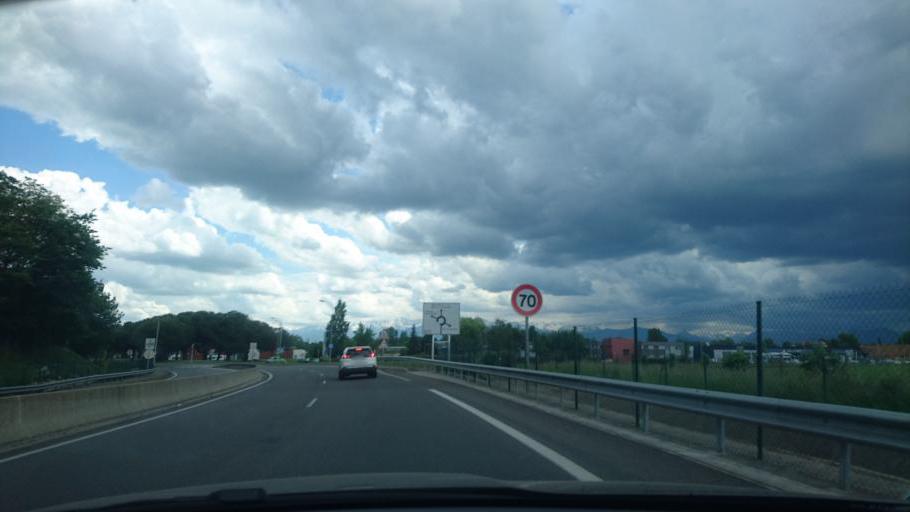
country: FR
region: Midi-Pyrenees
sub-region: Departement des Hautes-Pyrenees
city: Odos
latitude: 43.2245
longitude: 0.0453
